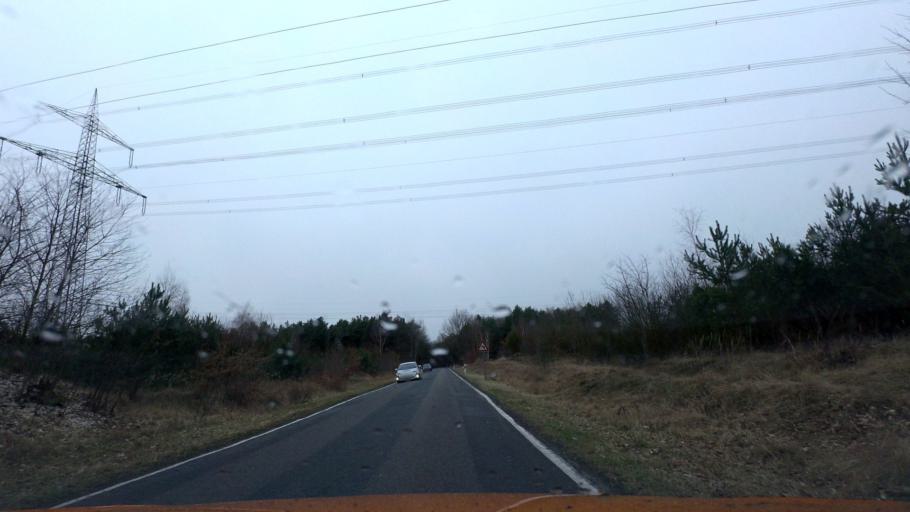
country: DE
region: Brandenburg
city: Falkensee
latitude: 52.6290
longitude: 13.0800
